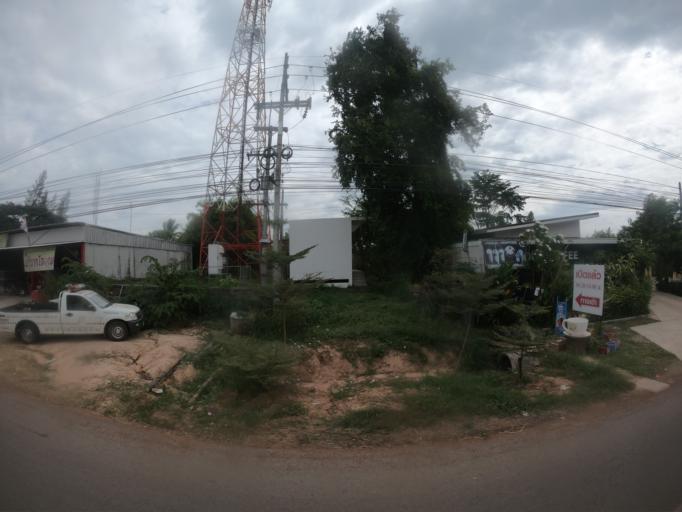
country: TH
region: Maha Sarakham
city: Kantharawichai
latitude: 16.3059
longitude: 103.2995
